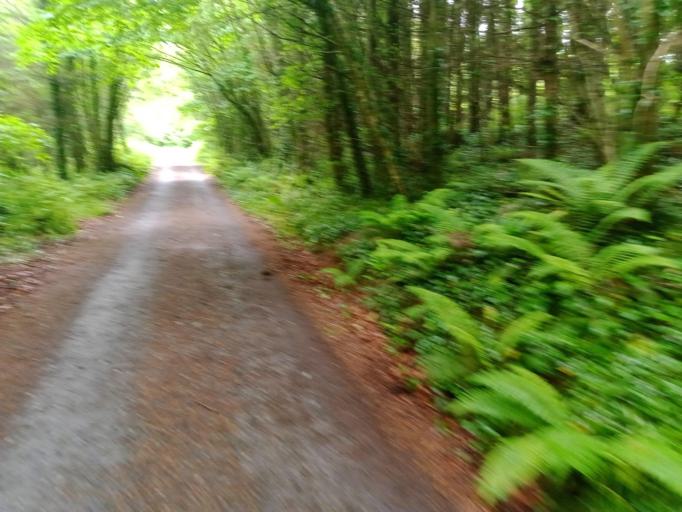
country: IE
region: Leinster
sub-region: Kilkenny
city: Thomastown
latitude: 52.4792
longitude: -7.0486
